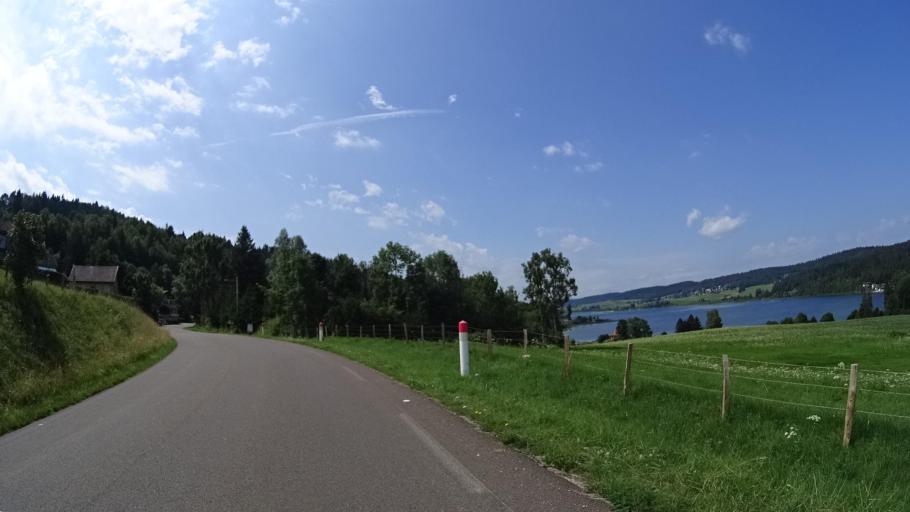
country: FR
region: Franche-Comte
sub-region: Departement du Doubs
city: Les Fourgs
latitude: 46.8350
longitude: 6.3442
